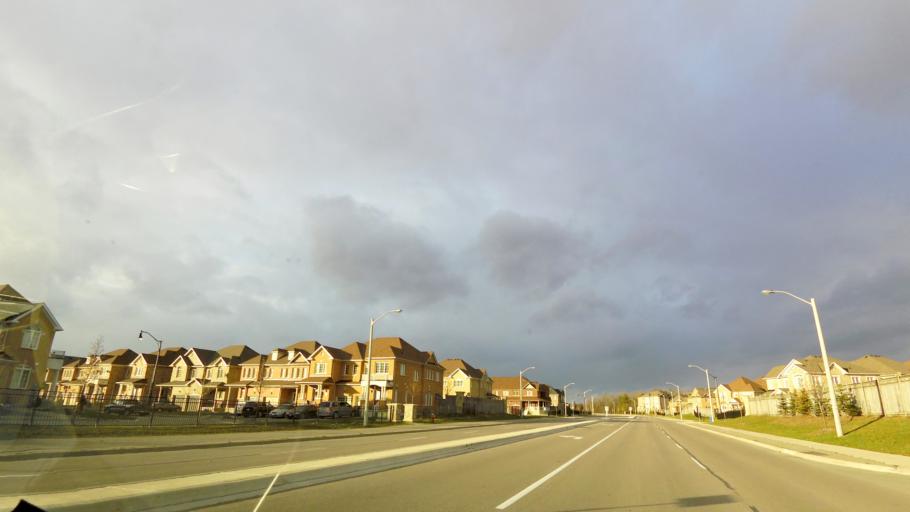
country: CA
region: Ontario
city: Brampton
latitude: 43.7871
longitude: -79.6639
